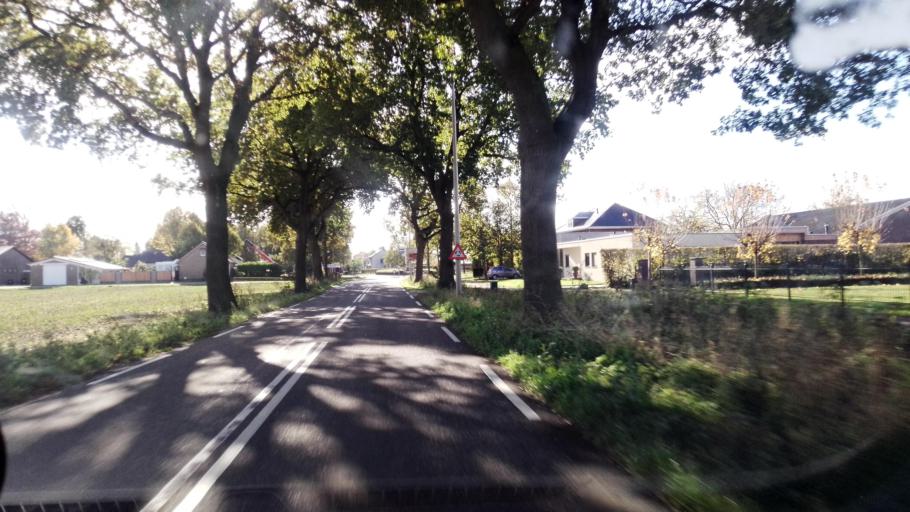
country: NL
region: Limburg
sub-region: Gemeente Venlo
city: Arcen
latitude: 51.4297
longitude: 6.1486
